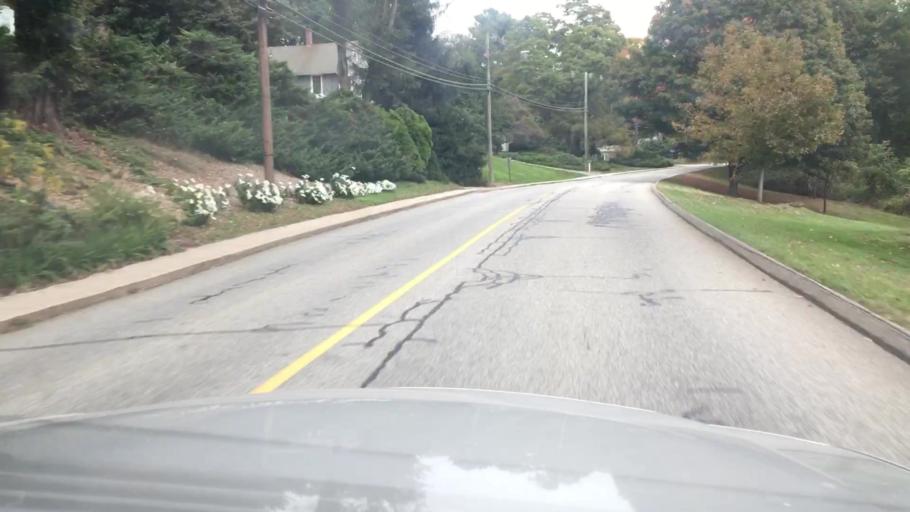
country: US
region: Connecticut
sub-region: Middlesex County
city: Essex Village
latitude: 41.3533
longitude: -72.4002
